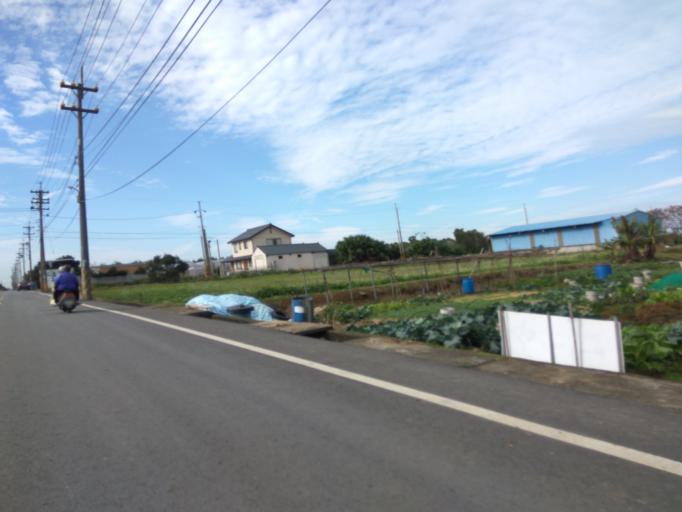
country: TW
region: Taiwan
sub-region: Hsinchu
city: Zhubei
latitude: 24.9920
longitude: 121.0919
